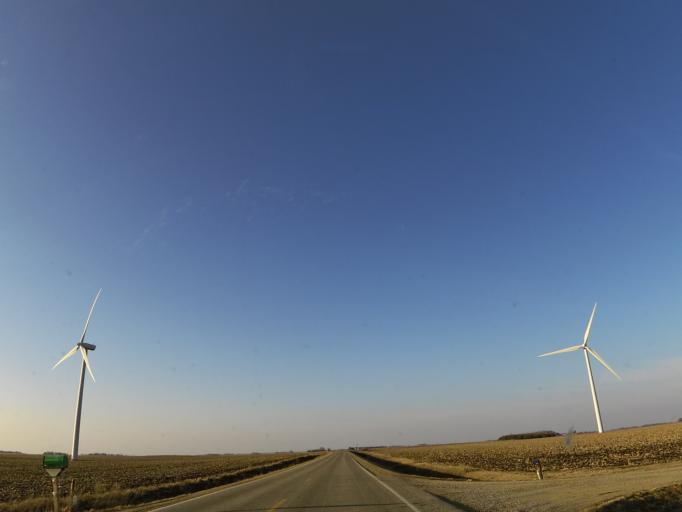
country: US
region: Iowa
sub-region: Worth County
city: Northwood
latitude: 43.4188
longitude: -93.1243
